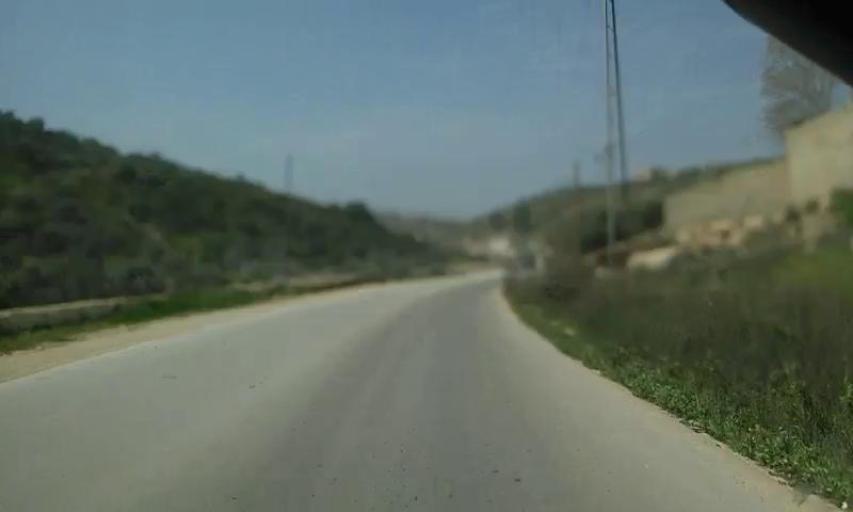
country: PS
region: West Bank
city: Qabatiyah
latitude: 32.4048
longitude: 35.2976
